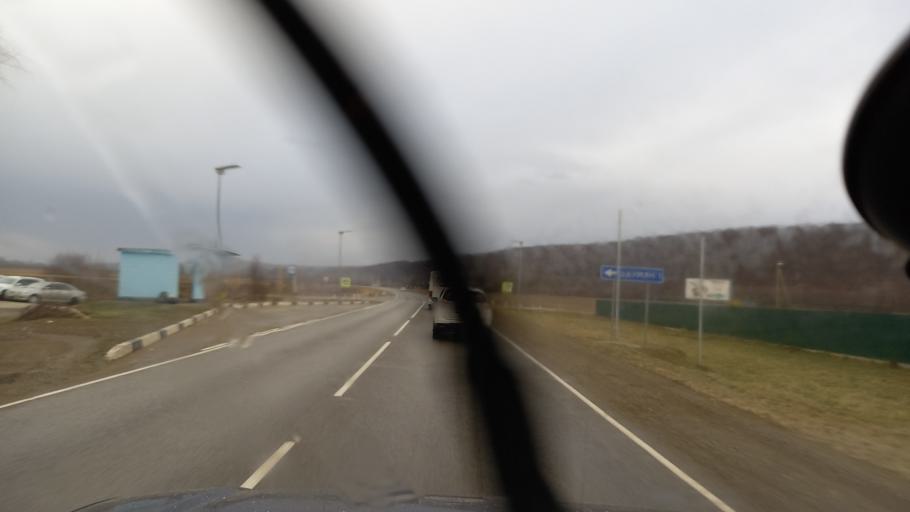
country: RU
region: Adygeya
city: Tul'skiy
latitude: 44.5268
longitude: 40.1360
